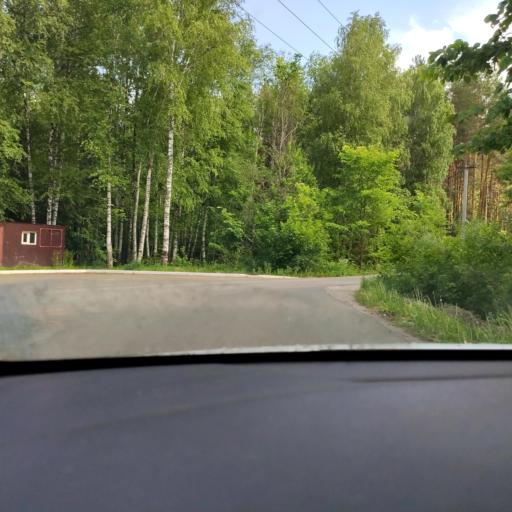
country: RU
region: Tatarstan
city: Vysokaya Gora
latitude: 55.9470
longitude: 49.2968
